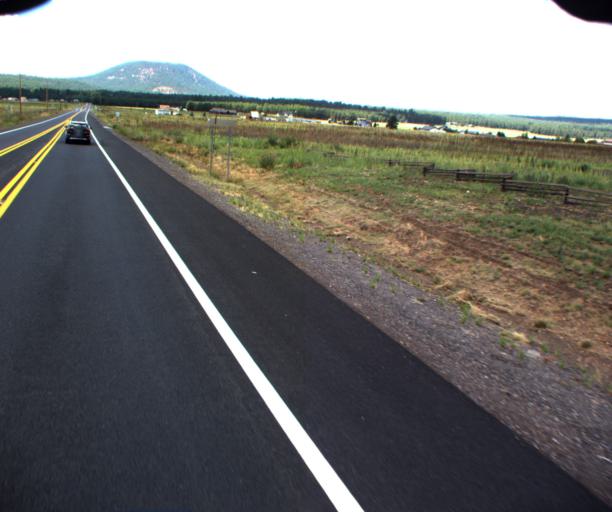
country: US
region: Arizona
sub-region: Coconino County
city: Flagstaff
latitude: 35.2685
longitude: -111.7201
